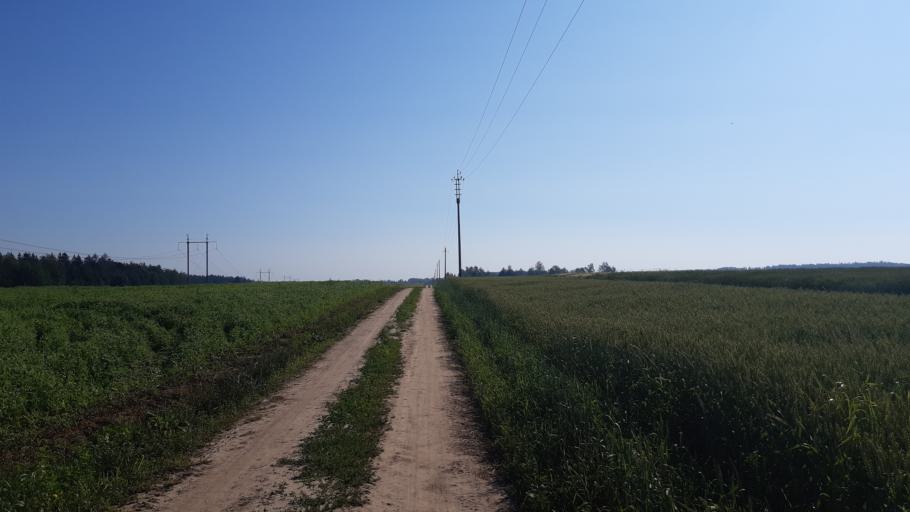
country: BY
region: Minsk
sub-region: Smalyavitski Rayon
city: Oktjabr'skij
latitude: 54.0855
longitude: 28.2174
